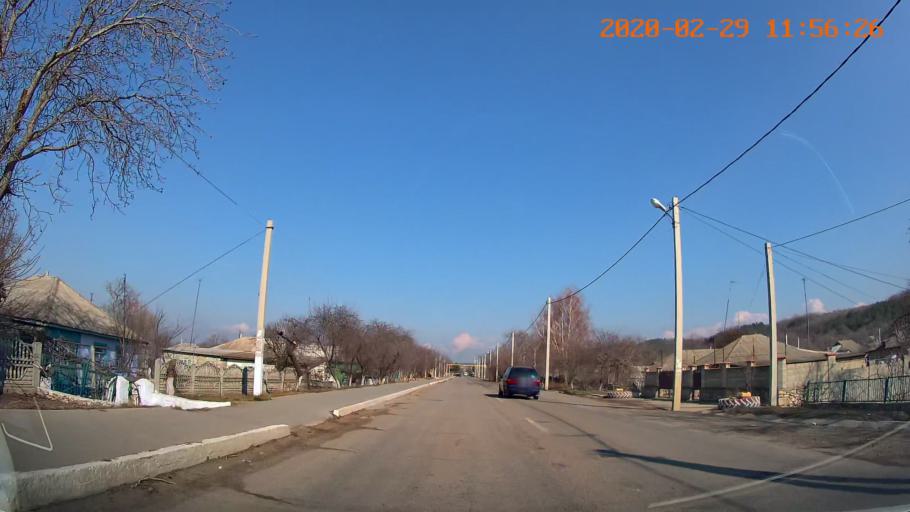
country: MD
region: Telenesti
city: Ribnita
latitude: 47.7966
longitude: 29.0019
